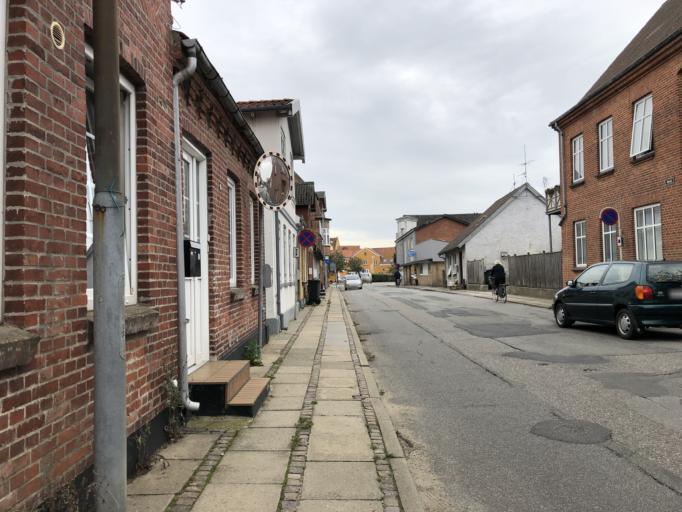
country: DK
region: North Denmark
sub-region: Morso Kommune
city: Nykobing Mors
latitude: 56.7959
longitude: 8.8547
